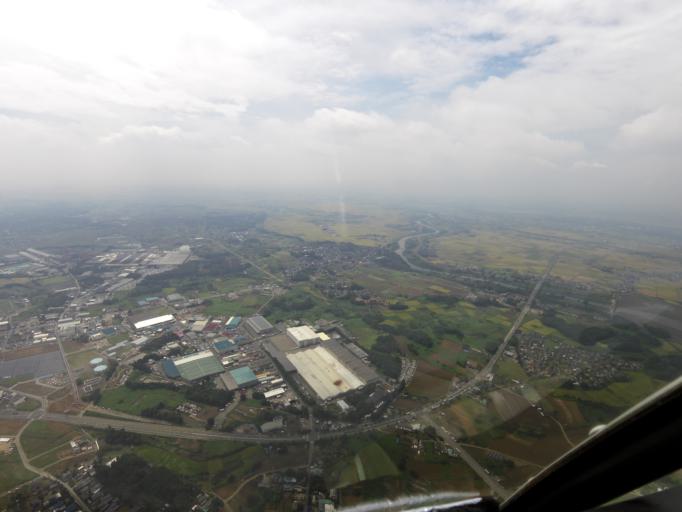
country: JP
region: Ibaraki
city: Mitsukaido
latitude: 36.0452
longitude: 140.0481
